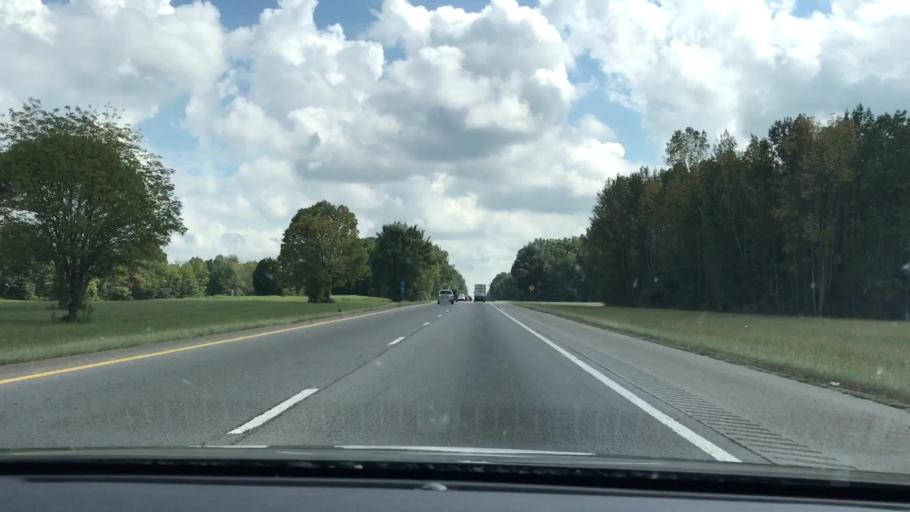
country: US
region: Tennessee
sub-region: Cheatham County
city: Pleasant View
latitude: 36.4491
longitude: -87.0984
